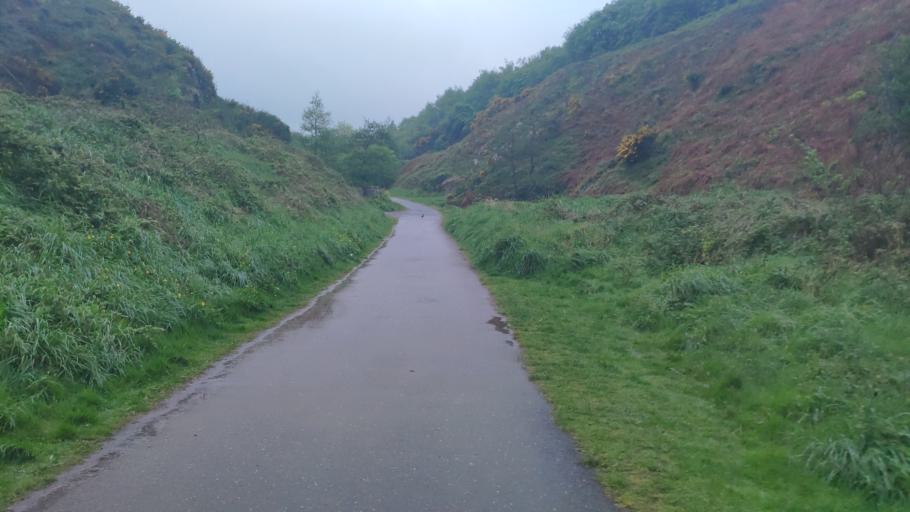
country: IE
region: Munster
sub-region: County Cork
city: Cork
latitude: 51.9138
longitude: -8.4624
